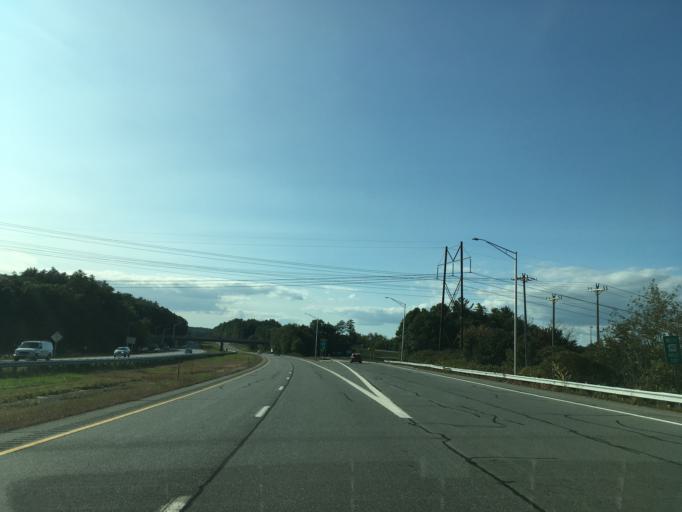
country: US
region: New Hampshire
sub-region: Rockingham County
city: Hampton
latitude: 42.9606
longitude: -70.8589
